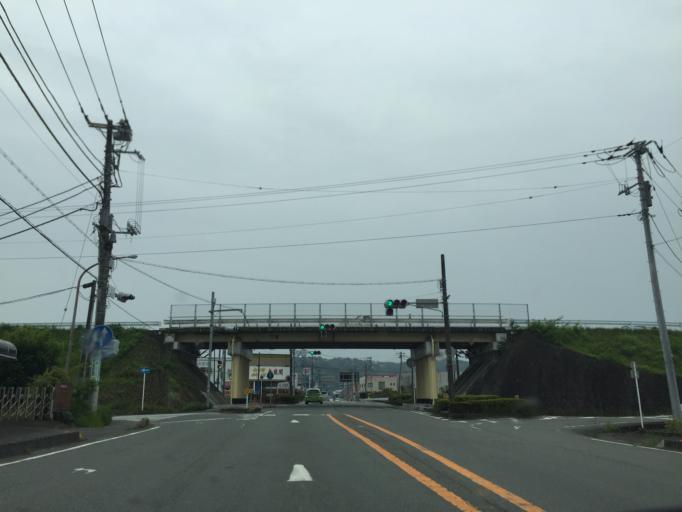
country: JP
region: Shizuoka
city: Mishima
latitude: 35.0106
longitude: 138.9433
